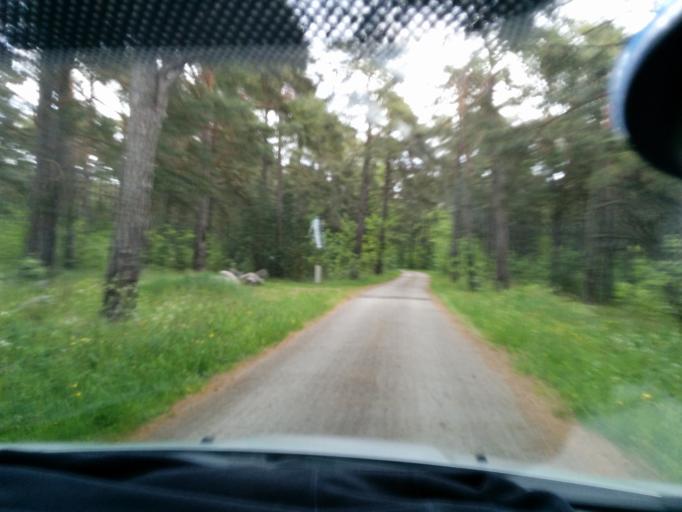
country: EE
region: Harju
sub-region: Loksa linn
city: Loksa
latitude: 59.6556
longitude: 25.6774
